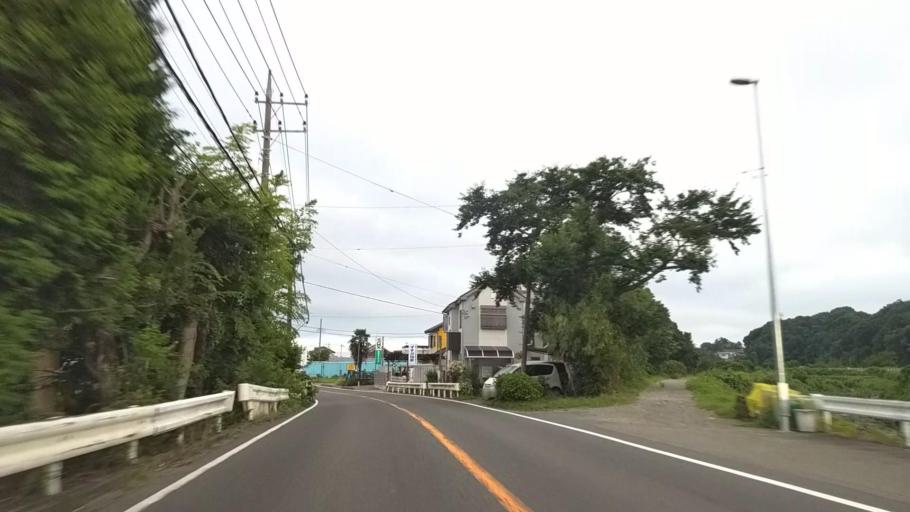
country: JP
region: Kanagawa
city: Atsugi
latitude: 35.4651
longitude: 139.3424
